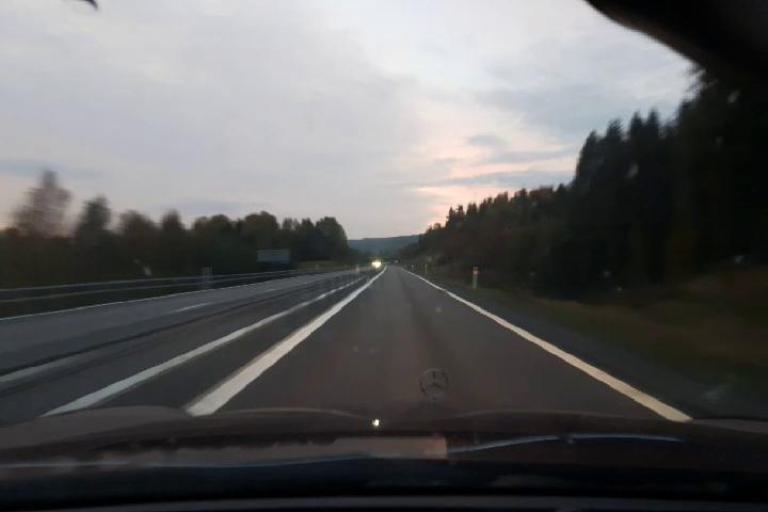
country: SE
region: Vaesternorrland
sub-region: Kramfors Kommun
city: Nordingra
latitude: 62.9335
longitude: 18.0952
